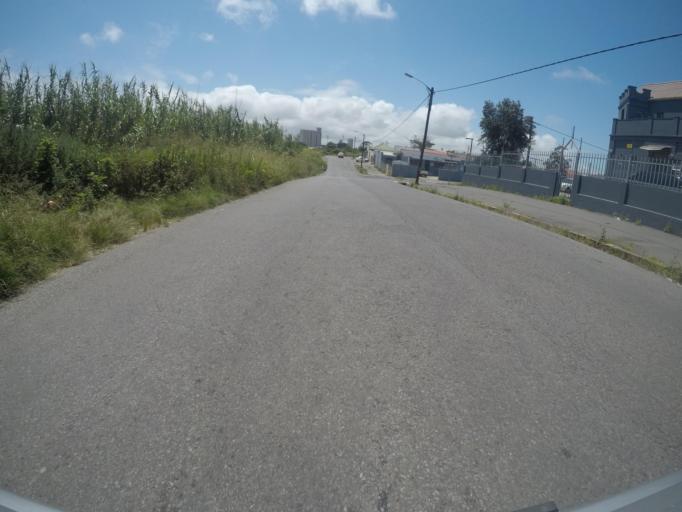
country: ZA
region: Eastern Cape
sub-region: Buffalo City Metropolitan Municipality
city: East London
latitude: -33.0146
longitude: 27.9104
